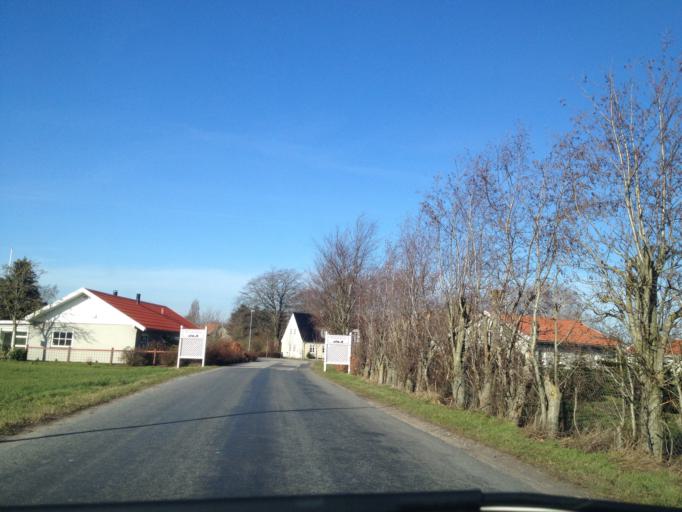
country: DK
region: South Denmark
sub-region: Nyborg Kommune
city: Ullerslev
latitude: 55.3837
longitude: 10.7117
